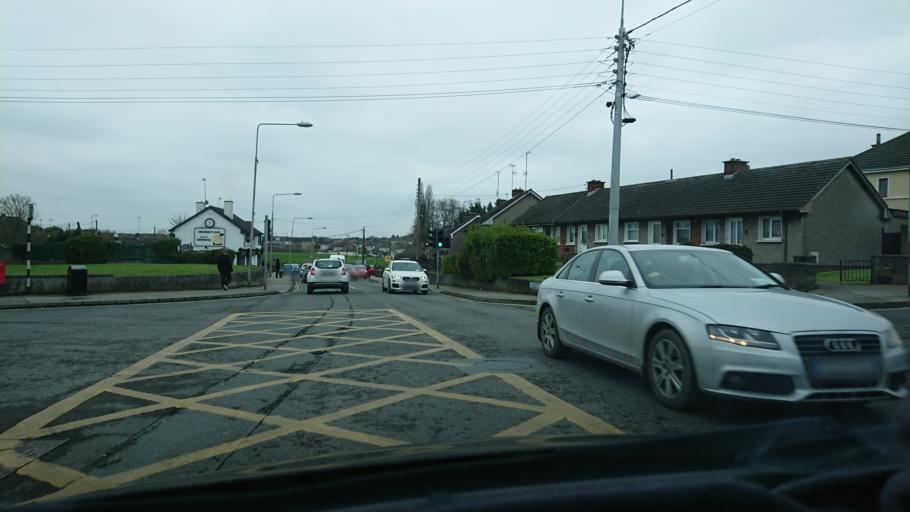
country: IE
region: Leinster
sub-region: Lu
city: Drogheda
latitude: 53.7201
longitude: -6.3413
